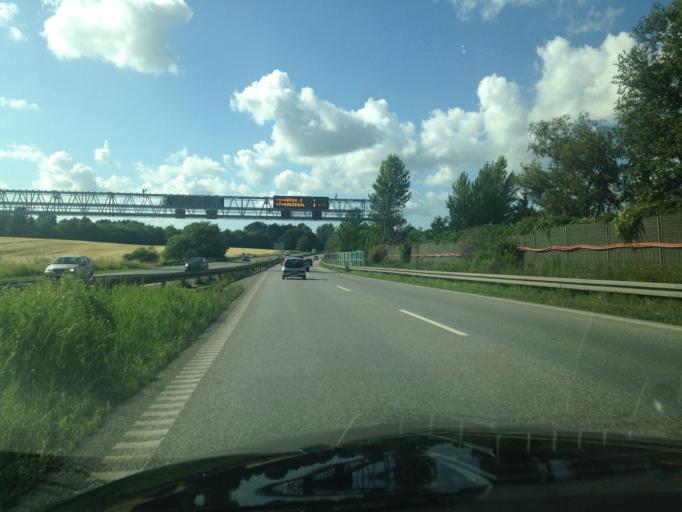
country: DK
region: Capital Region
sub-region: Horsholm Kommune
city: Horsholm
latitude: 55.8613
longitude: 12.4910
